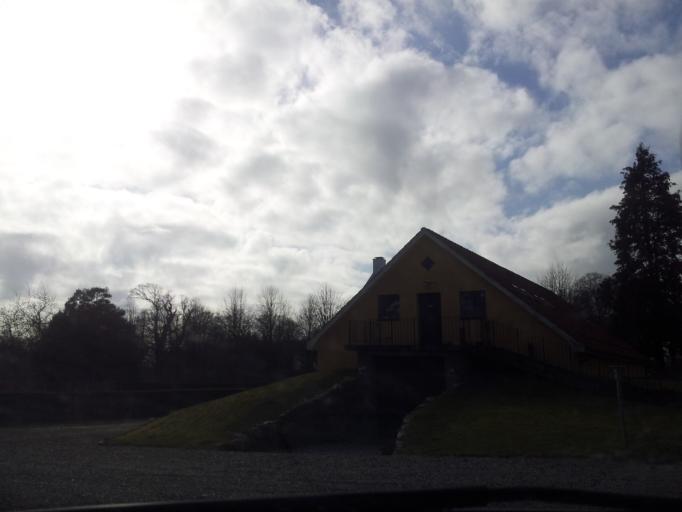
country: DK
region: South Denmark
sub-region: Vejen Kommune
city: Brorup
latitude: 55.4521
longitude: 9.0392
